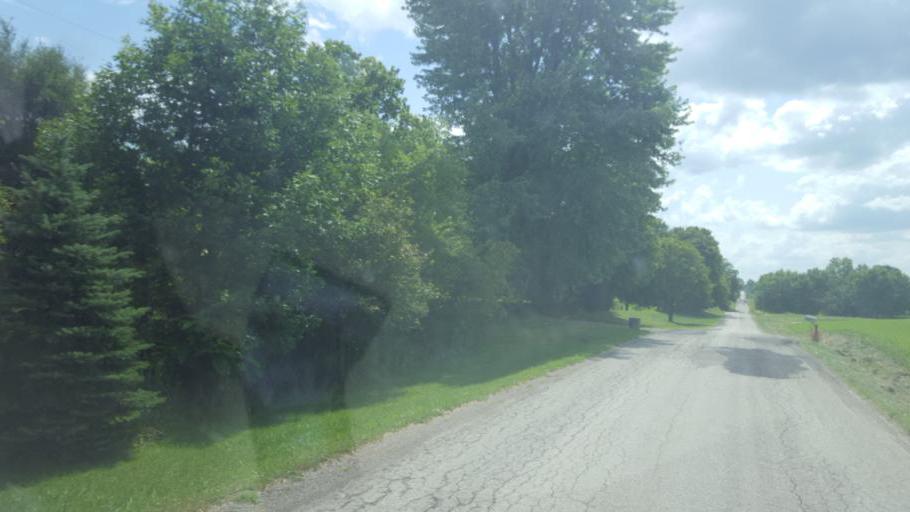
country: US
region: Ohio
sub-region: Knox County
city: Centerburg
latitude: 40.3688
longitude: -82.8039
